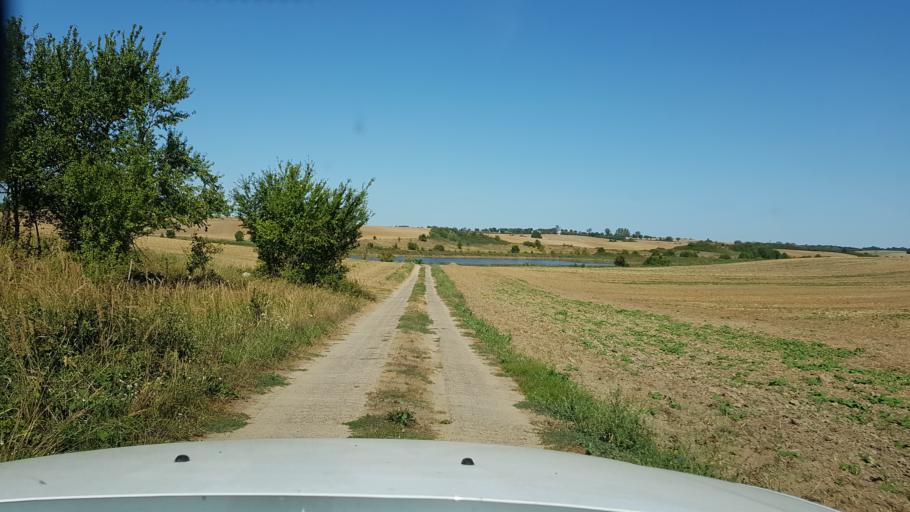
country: PL
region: West Pomeranian Voivodeship
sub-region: Powiat gryfinski
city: Moryn
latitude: 52.8464
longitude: 14.3615
